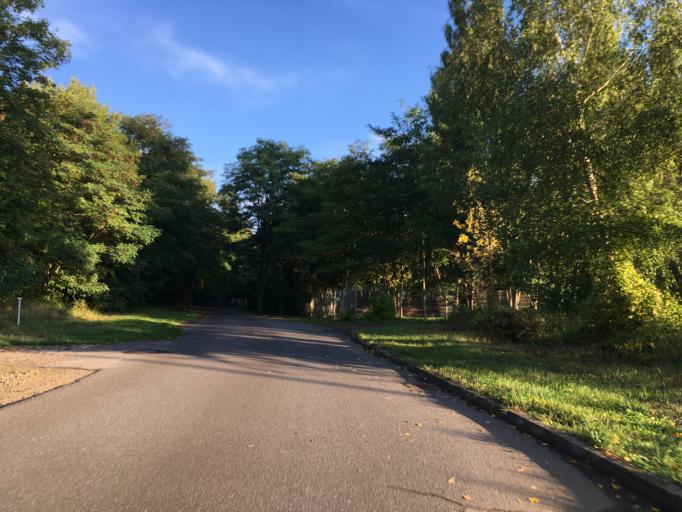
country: DE
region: Brandenburg
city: Frankfurt (Oder)
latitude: 52.3601
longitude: 14.5485
